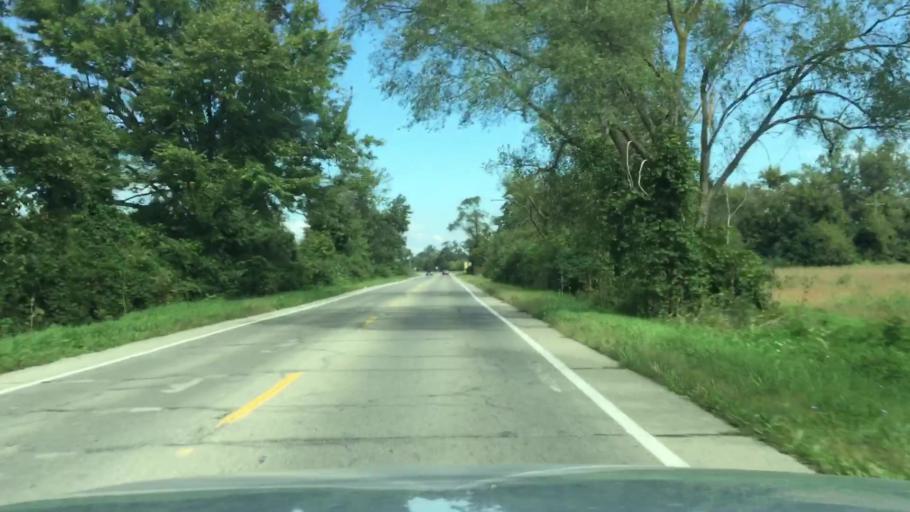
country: US
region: Michigan
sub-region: Wayne County
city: Belleville
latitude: 42.1866
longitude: -83.4833
